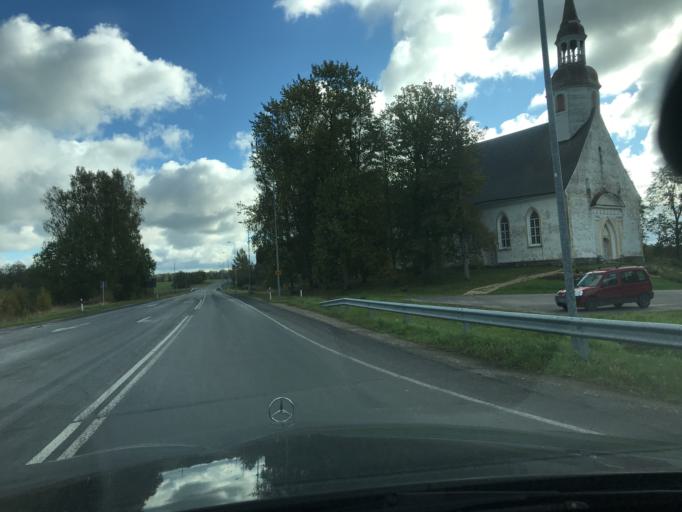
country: EE
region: Vorumaa
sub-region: Antsla vald
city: Vana-Antsla
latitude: 57.9265
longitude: 26.3324
